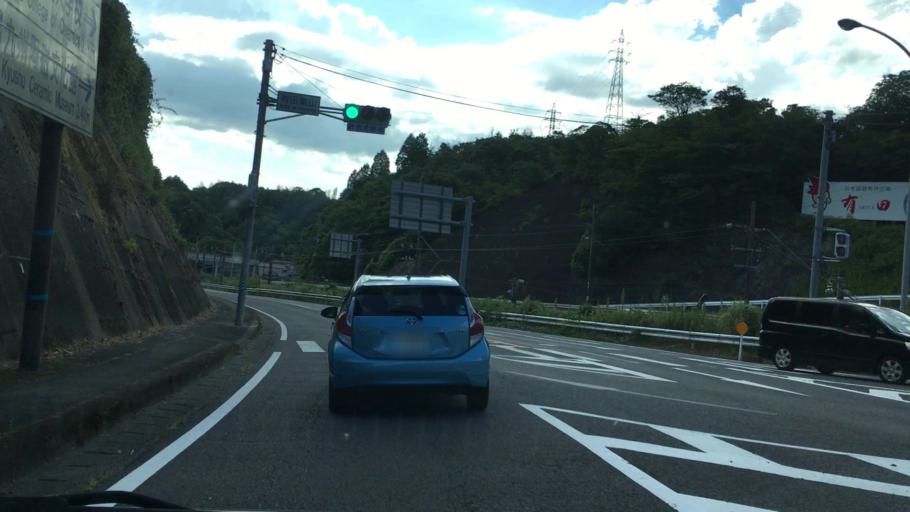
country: JP
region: Saga Prefecture
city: Imaricho-ko
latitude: 33.1918
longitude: 129.9115
